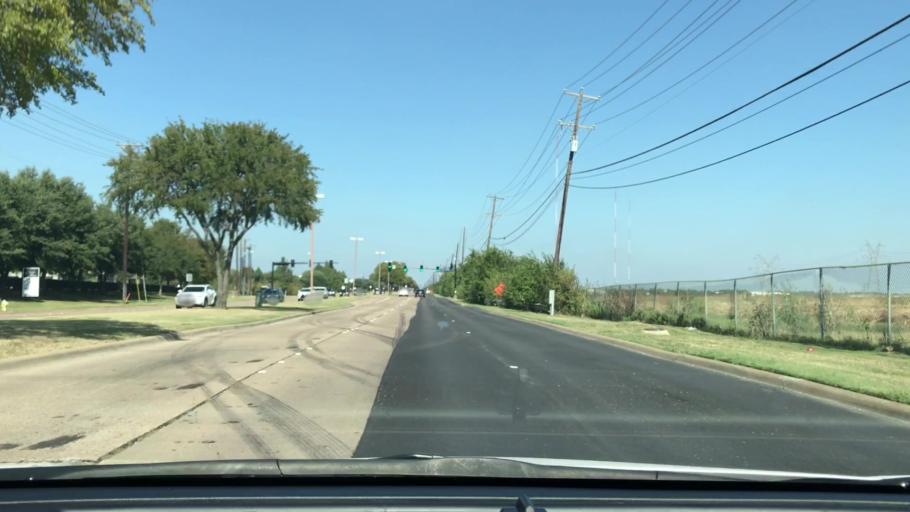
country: US
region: Texas
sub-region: Dallas County
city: Coppell
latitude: 32.9338
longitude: -96.9935
